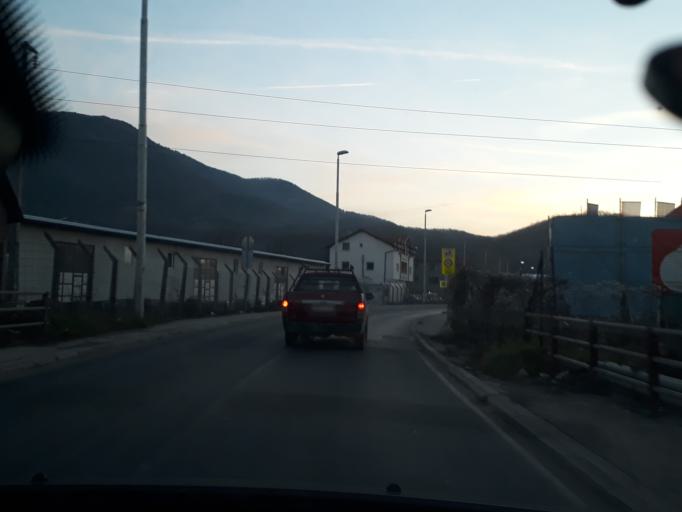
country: BA
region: Federation of Bosnia and Herzegovina
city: Hadzici
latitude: 43.8492
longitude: 18.2478
